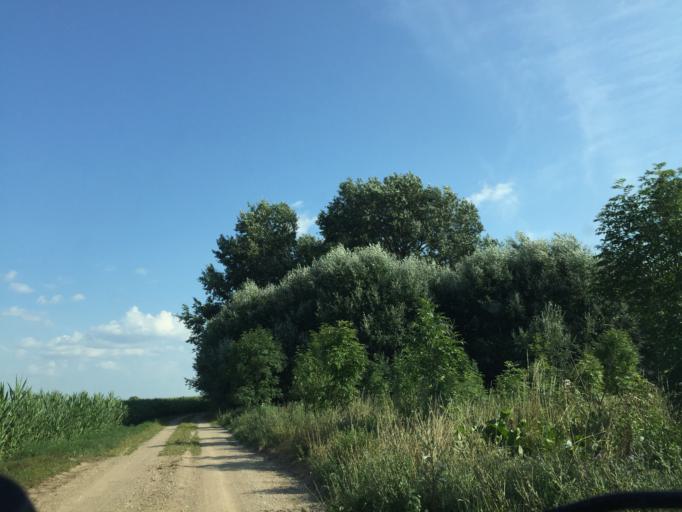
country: LV
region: Jelgava
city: Jelgava
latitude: 56.4697
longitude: 23.6746
